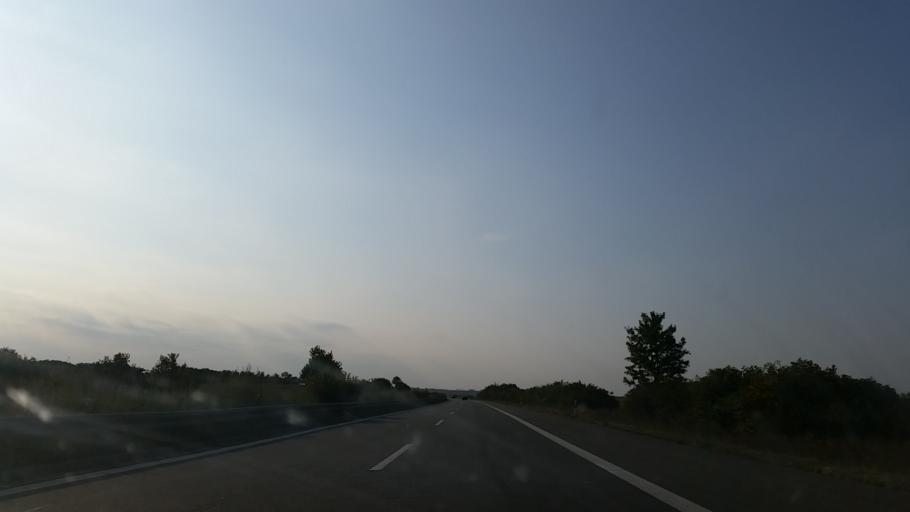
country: DE
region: Mecklenburg-Vorpommern
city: Neuenkirchen
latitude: 53.5726
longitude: 13.4564
